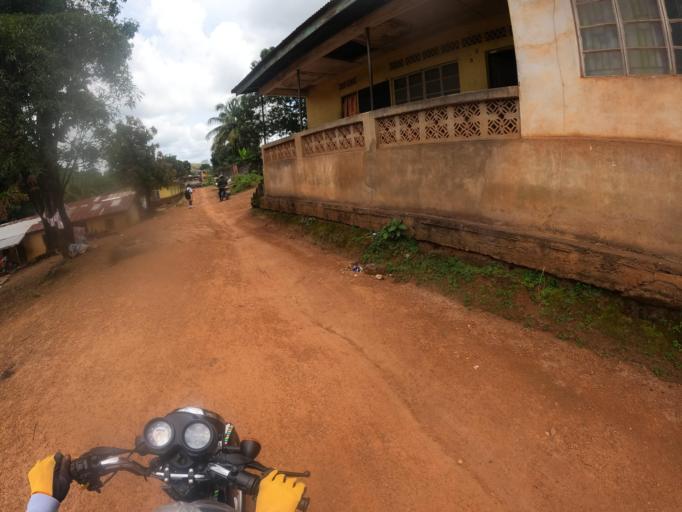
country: SL
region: Northern Province
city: Makeni
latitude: 8.8943
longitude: -12.0510
